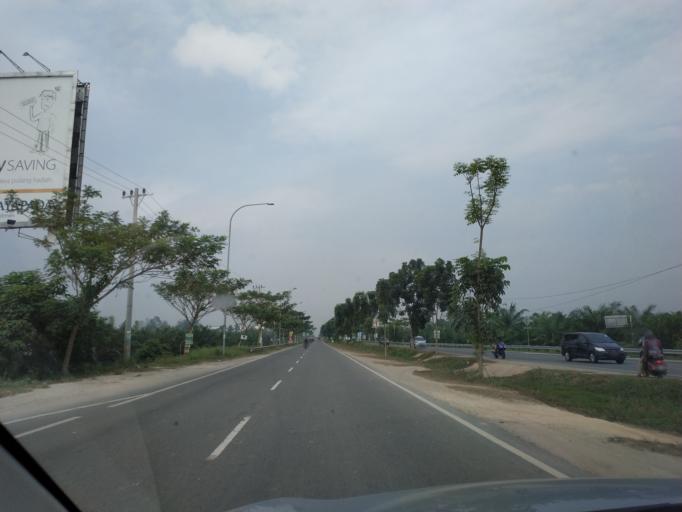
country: ID
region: North Sumatra
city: Percut
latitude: 3.5988
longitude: 98.8386
